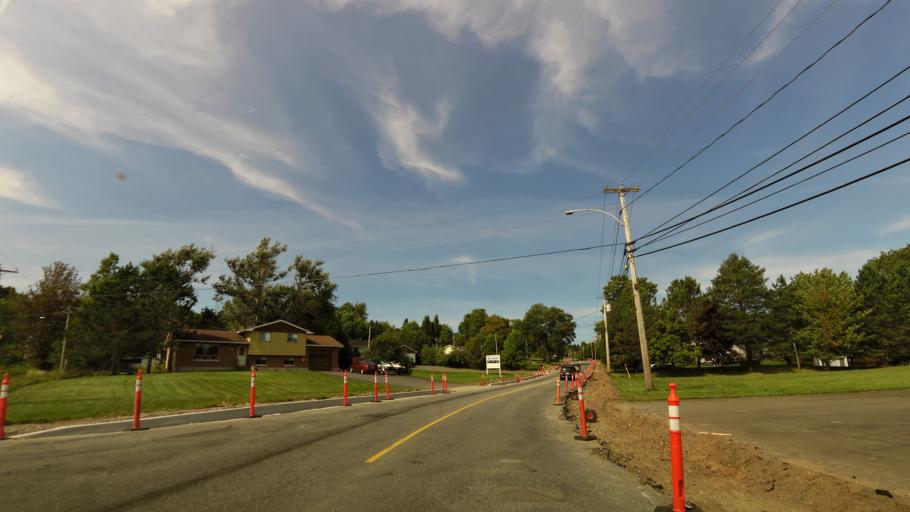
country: CA
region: New Brunswick
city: Hampton
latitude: 45.5278
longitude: -65.8311
